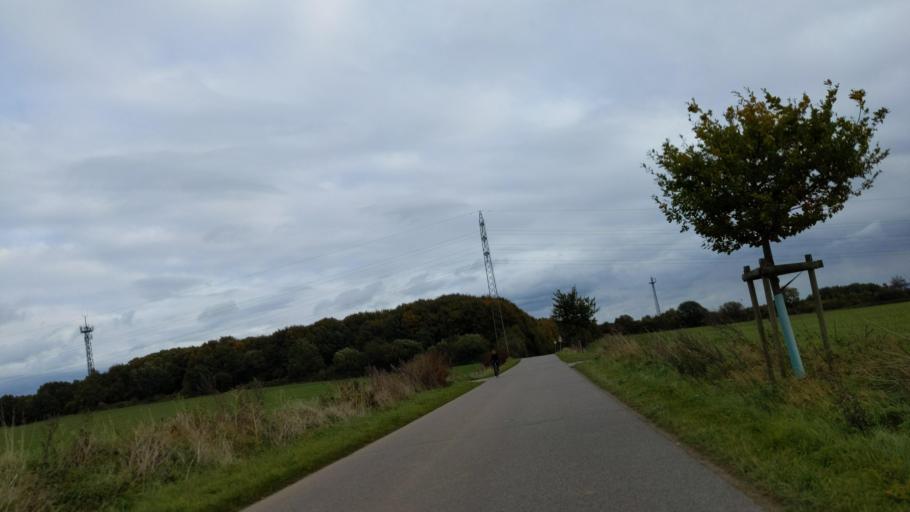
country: DE
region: Schleswig-Holstein
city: Sierksdorf
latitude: 54.0682
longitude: 10.7475
